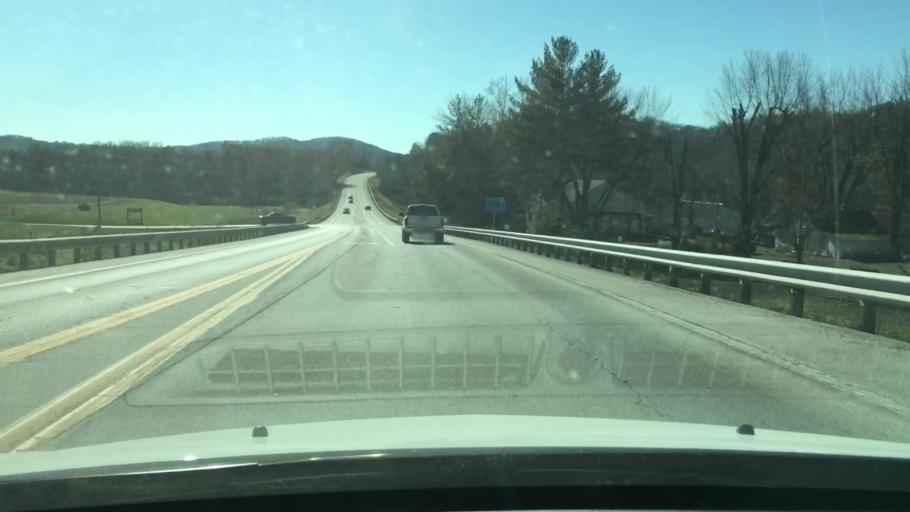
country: US
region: Missouri
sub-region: Pike County
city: Louisiana
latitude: 39.4389
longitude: -91.0794
